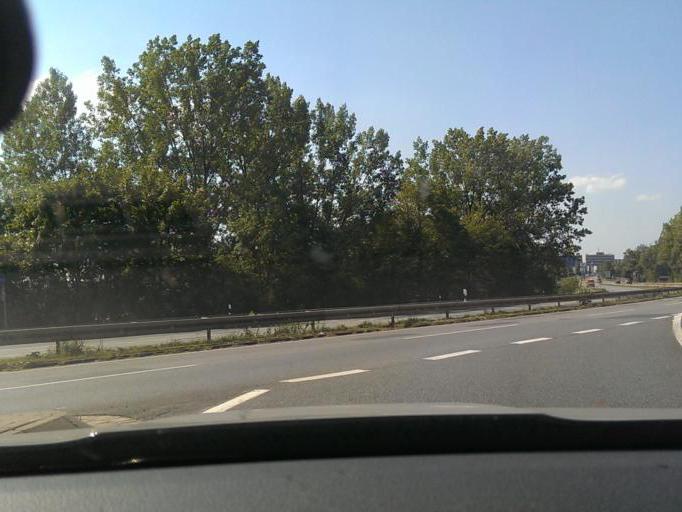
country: DE
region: Lower Saxony
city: Langenhagen
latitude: 52.4590
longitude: 9.7204
